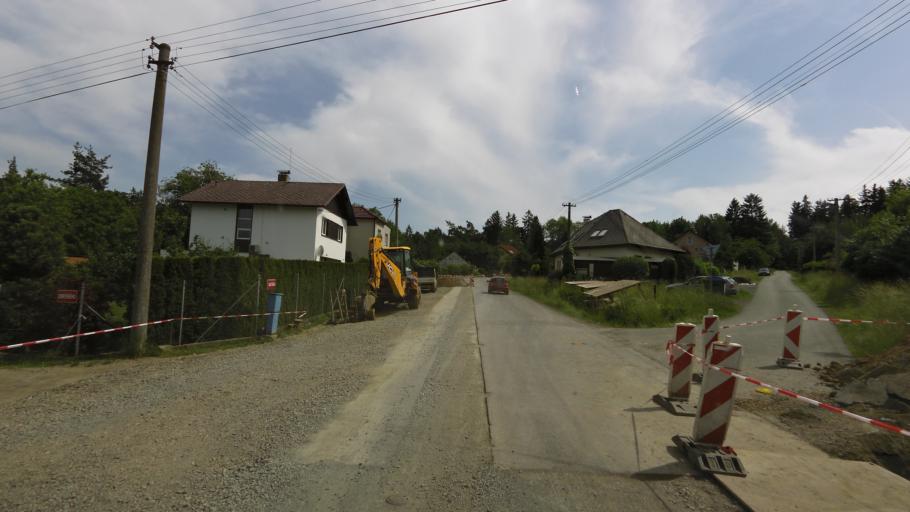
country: CZ
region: Plzensky
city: Stary Plzenec
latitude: 49.6871
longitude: 13.4762
